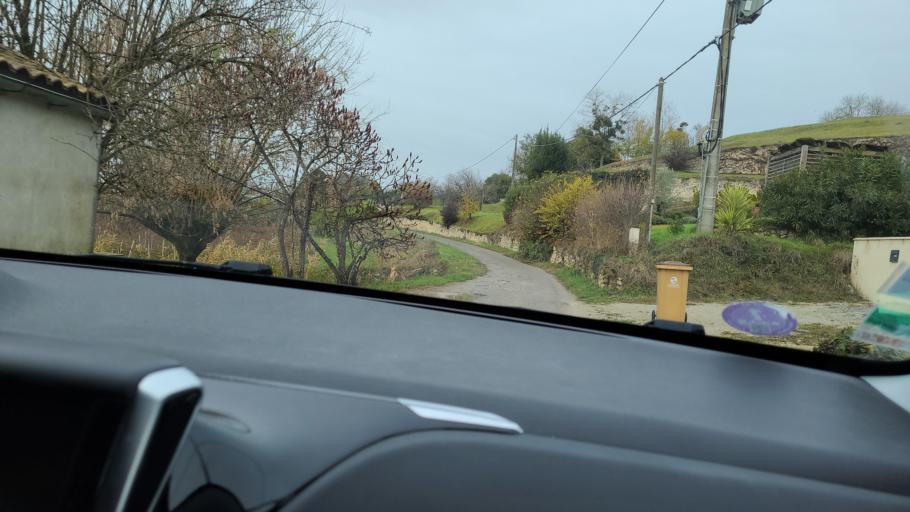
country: FR
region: Aquitaine
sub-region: Departement de la Gironde
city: Bourg
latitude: 45.0427
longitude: -0.5730
